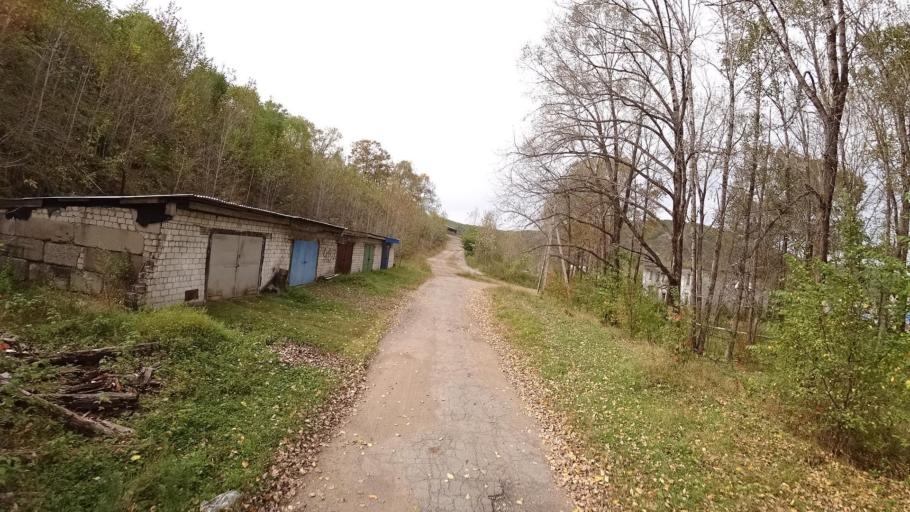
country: RU
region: Jewish Autonomous Oblast
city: Khingansk
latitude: 49.1243
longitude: 131.1979
